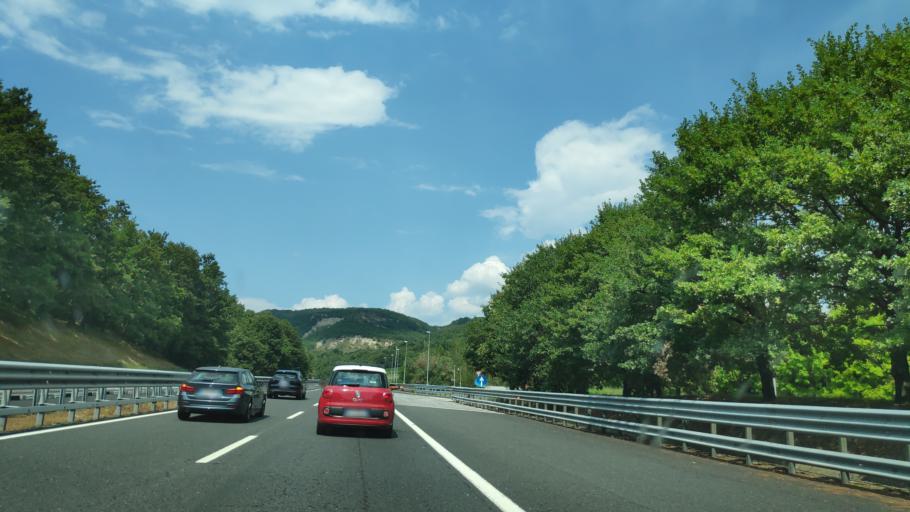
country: IT
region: Umbria
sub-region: Provincia di Terni
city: Stazione di Allerona
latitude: 42.7938
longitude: 12.0475
